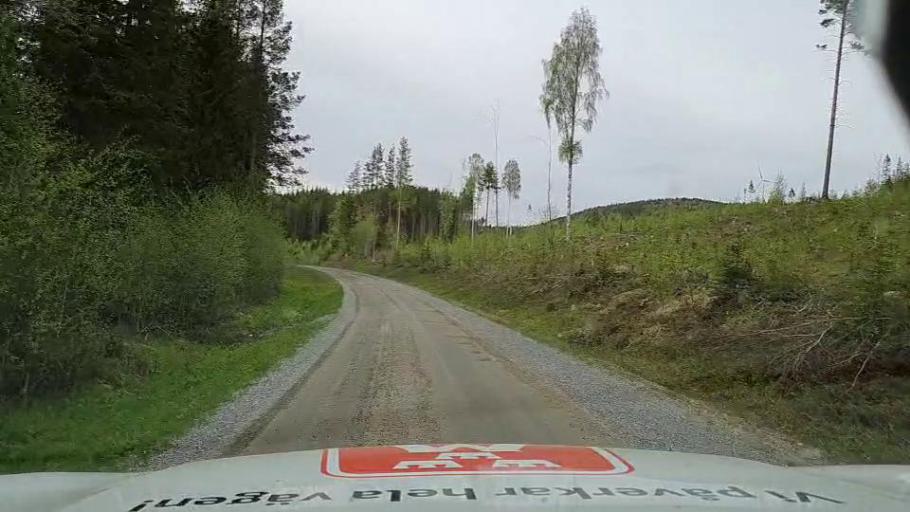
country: SE
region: Jaemtland
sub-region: Bergs Kommun
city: Hoverberg
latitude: 62.5289
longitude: 14.9156
